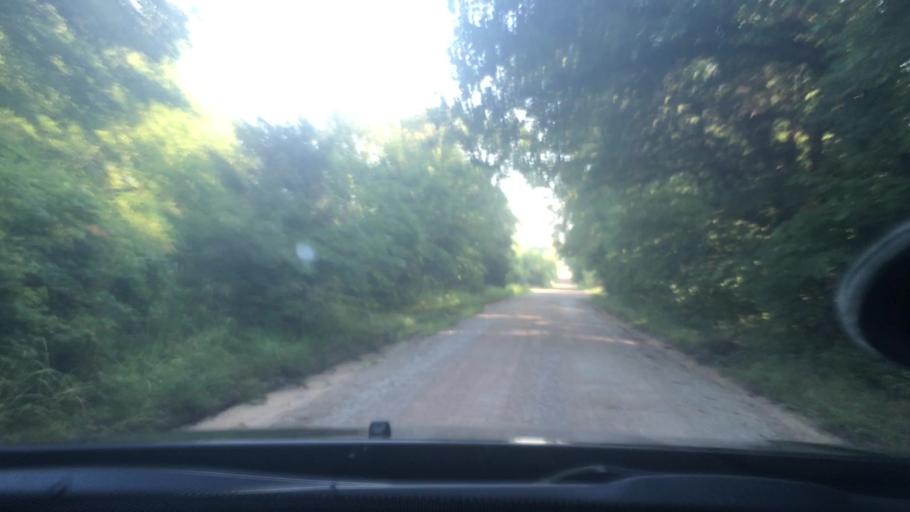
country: US
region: Oklahoma
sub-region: Pontotoc County
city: Ada
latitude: 34.8102
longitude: -96.7749
